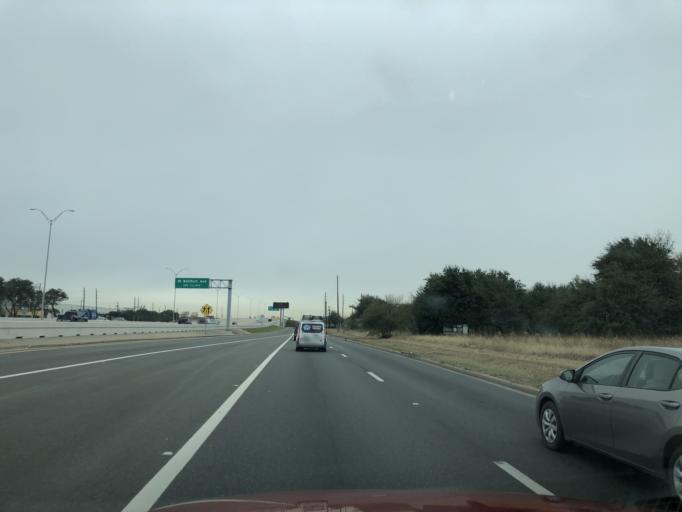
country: US
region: Texas
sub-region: Fort Bend County
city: Missouri City
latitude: 29.6408
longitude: -95.5346
